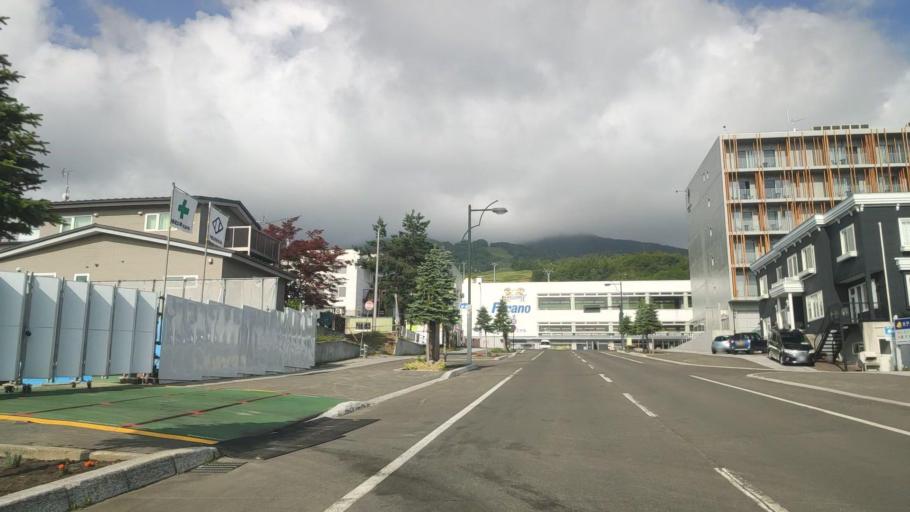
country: JP
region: Hokkaido
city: Shimo-furano
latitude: 43.3434
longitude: 142.3617
